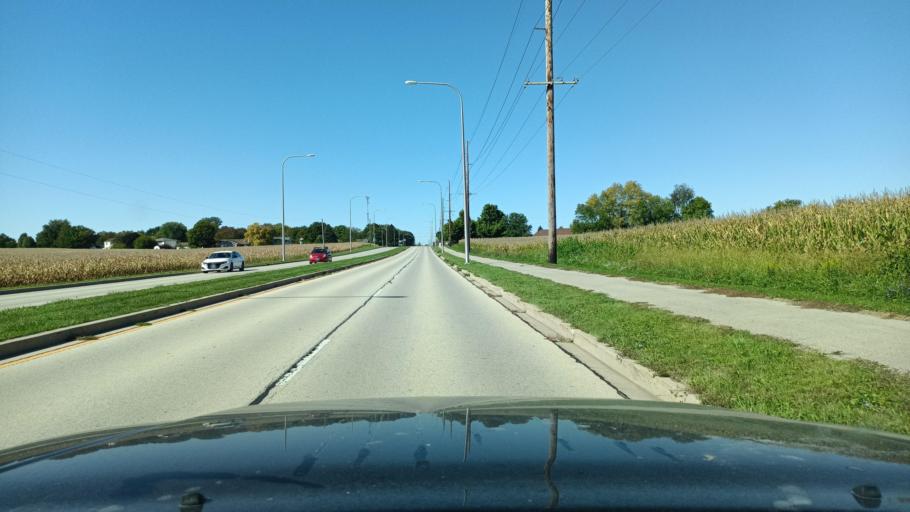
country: US
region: Illinois
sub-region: Champaign County
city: Urbana
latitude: 40.0840
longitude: -88.1770
